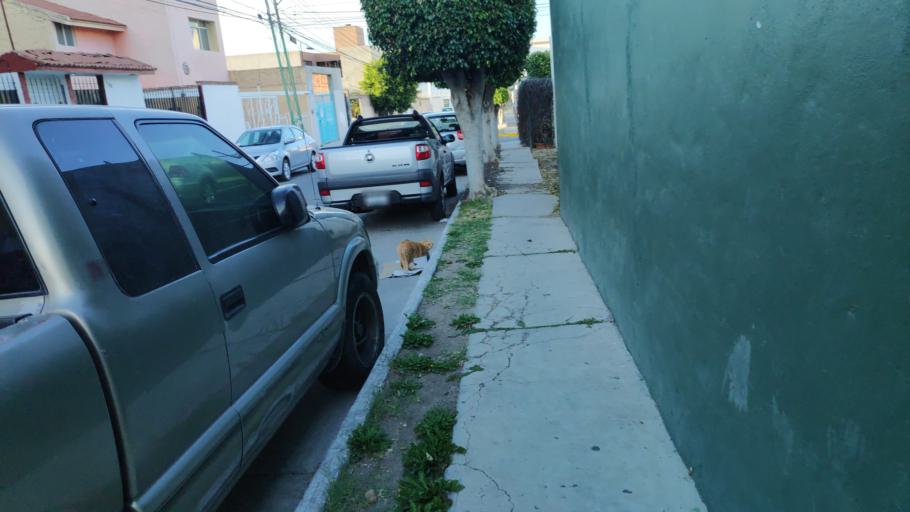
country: MX
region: Queretaro
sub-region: Queretaro
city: Santiago de Queretaro
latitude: 20.5810
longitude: -100.3822
